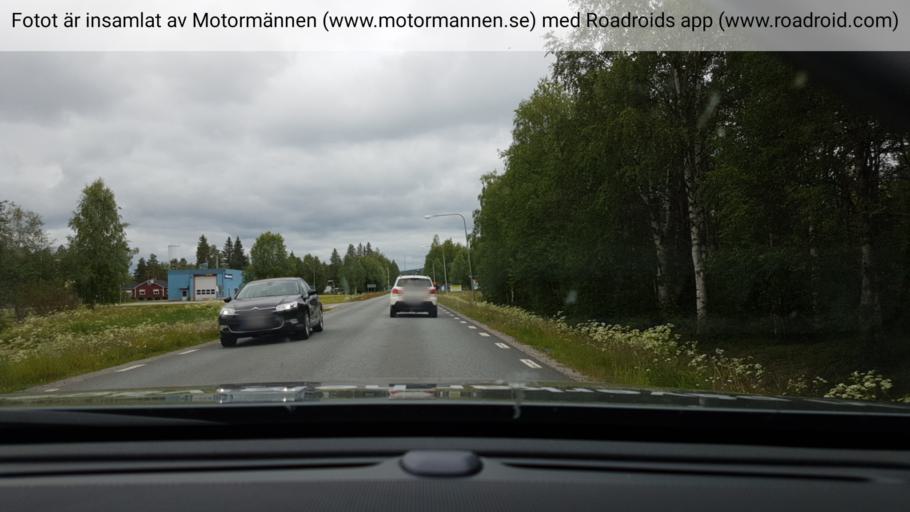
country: SE
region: Vaesterbotten
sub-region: Sorsele Kommun
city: Sorsele
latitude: 65.5234
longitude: 17.5387
